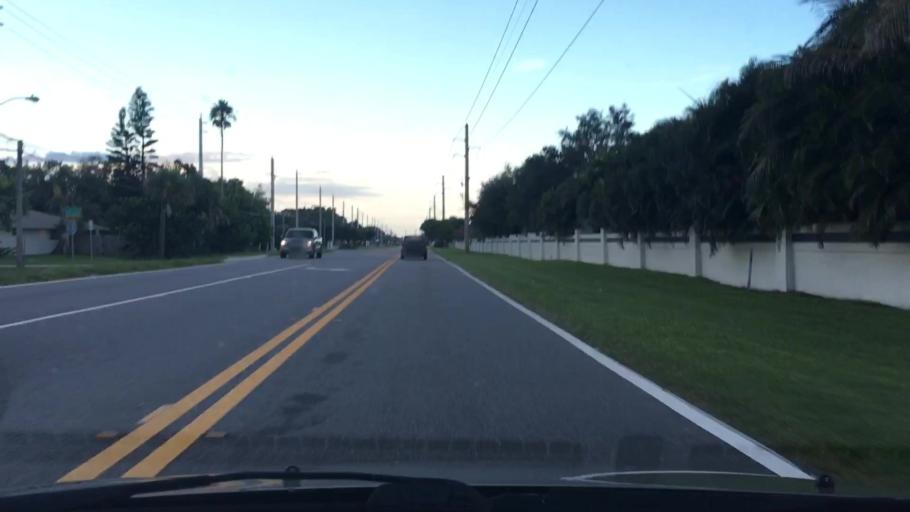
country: US
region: Florida
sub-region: Brevard County
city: Indian Harbour Beach
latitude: 28.1216
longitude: -80.5881
